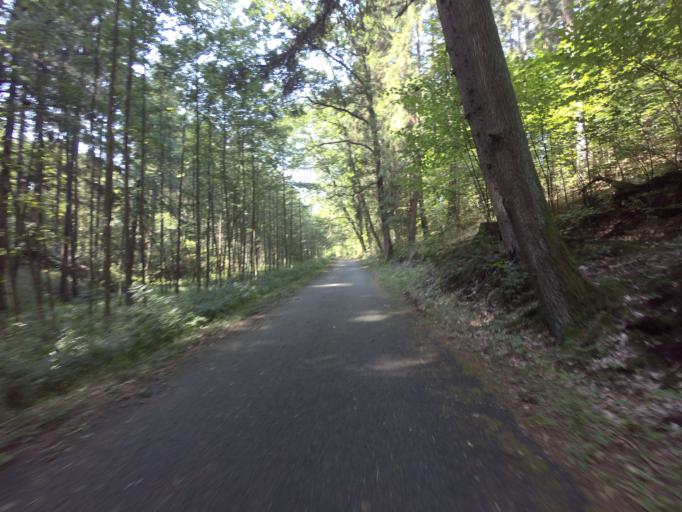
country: CZ
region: Jihocesky
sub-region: Okres Ceske Budejovice
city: Hluboka nad Vltavou
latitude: 49.1115
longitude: 14.4580
